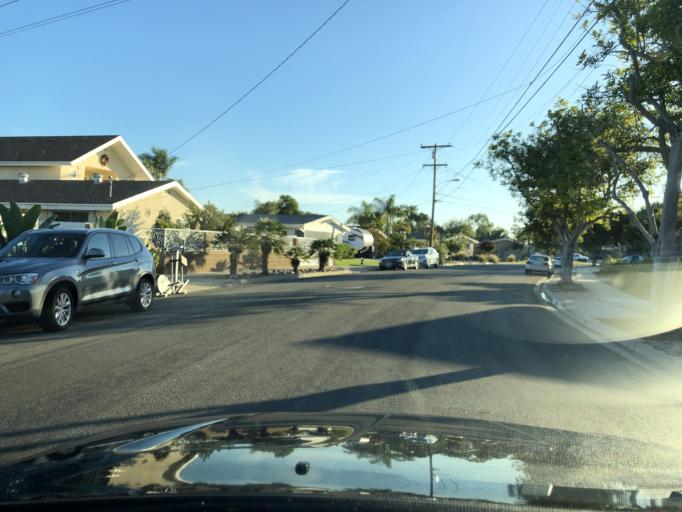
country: US
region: California
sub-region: San Diego County
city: La Jolla
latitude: 32.8161
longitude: -117.1950
